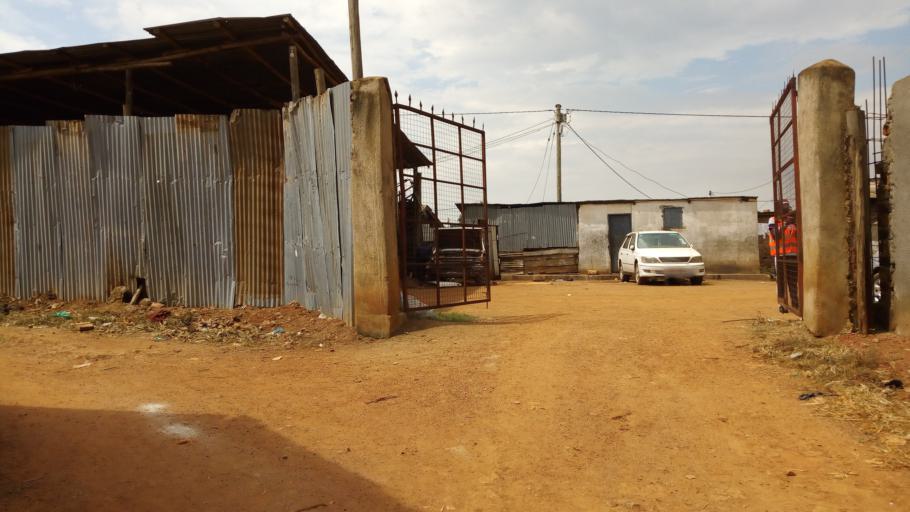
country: UG
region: Central Region
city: Kampala Central Division
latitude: 0.3512
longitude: 32.5613
